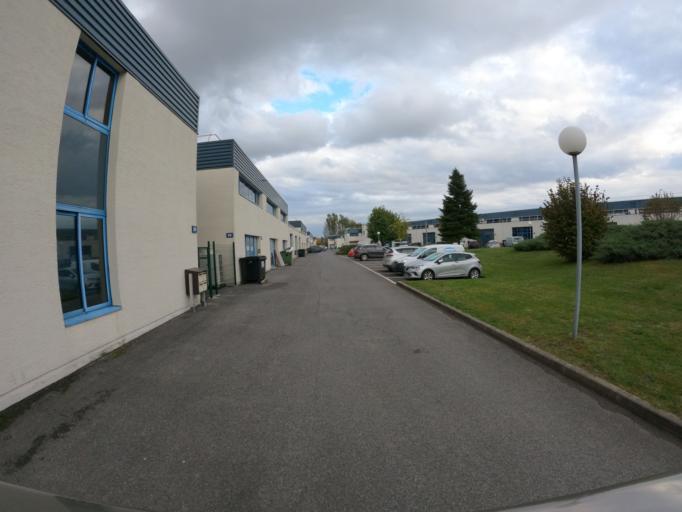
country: FR
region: Ile-de-France
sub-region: Departement de Seine-et-Marne
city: Lognes
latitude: 48.8242
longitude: 2.6318
